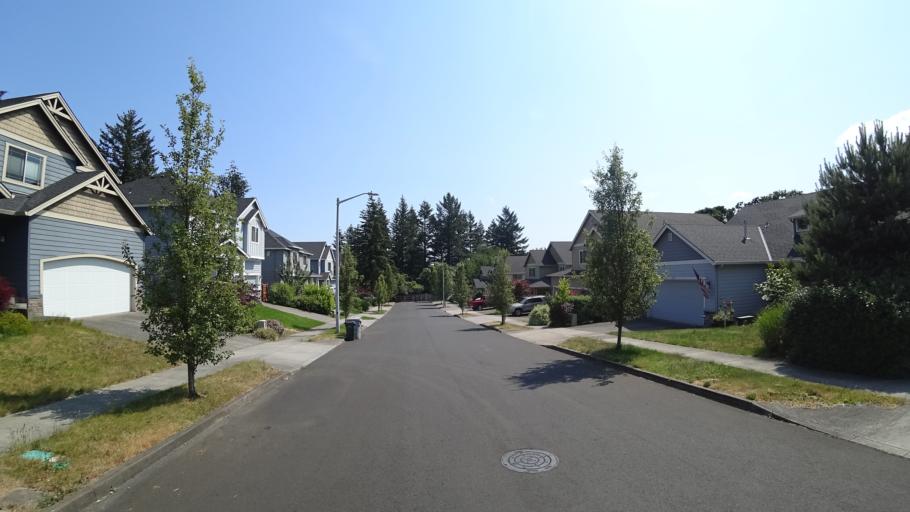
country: US
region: Oregon
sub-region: Clackamas County
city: Happy Valley
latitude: 45.4428
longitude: -122.5608
